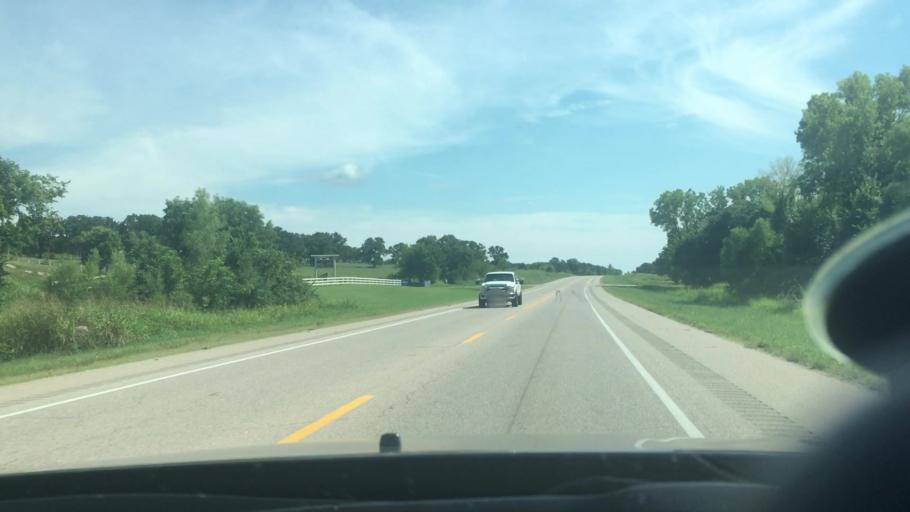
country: US
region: Oklahoma
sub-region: Seminole County
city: Seminole
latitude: 35.1757
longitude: -96.6742
